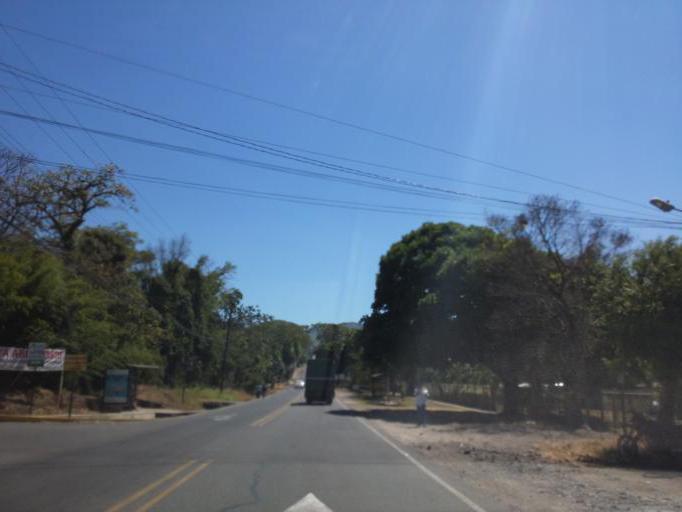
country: CR
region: Heredia
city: Colon
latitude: 9.9205
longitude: -84.2414
